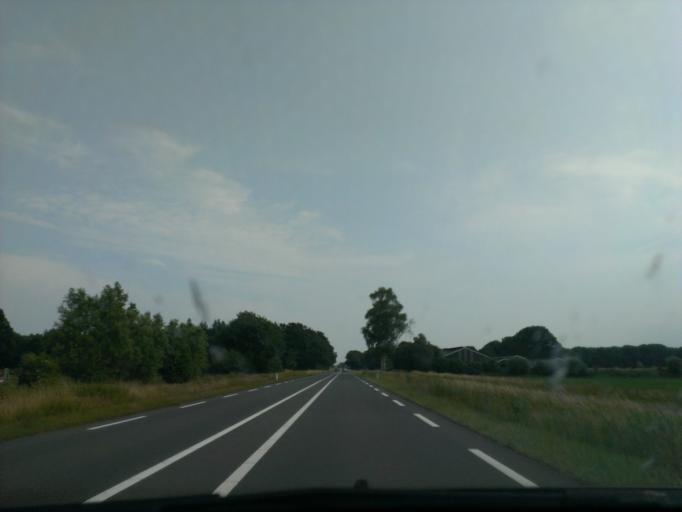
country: NL
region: Overijssel
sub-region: Gemeente Hof van Twente
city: Markelo
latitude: 52.2704
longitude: 6.4463
